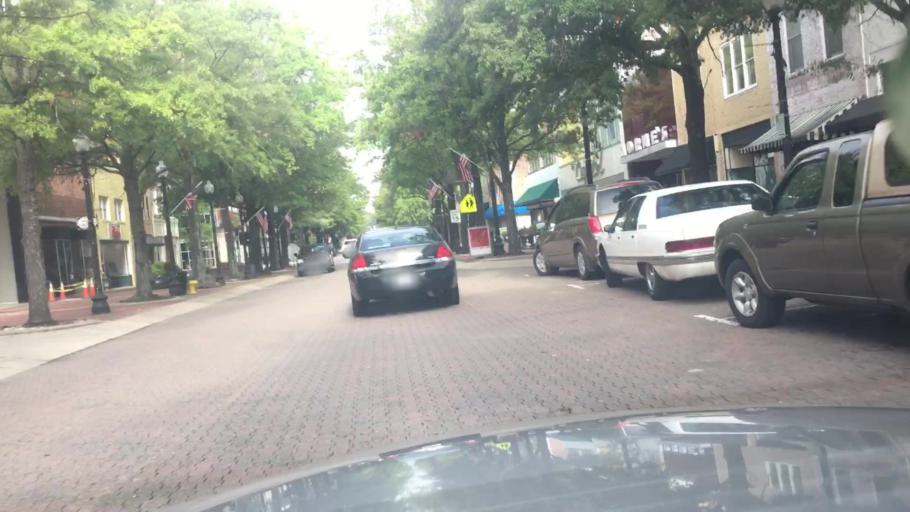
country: US
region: North Carolina
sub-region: Cumberland County
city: Fayetteville
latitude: 35.0528
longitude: -78.8788
